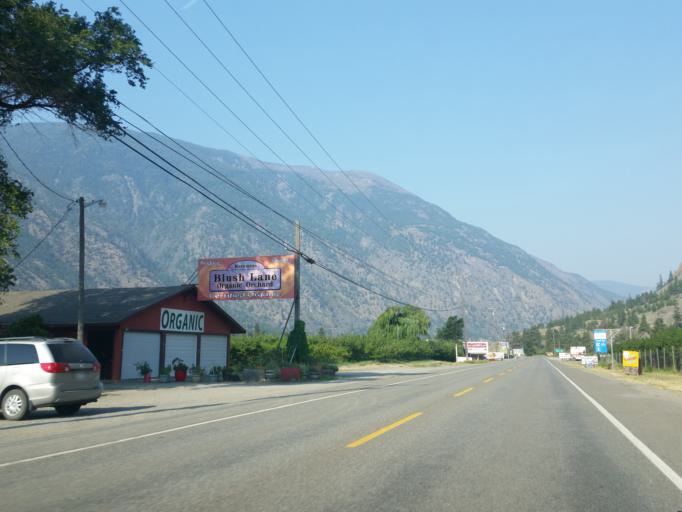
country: CA
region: British Columbia
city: Oliver
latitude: 49.2053
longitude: -119.8516
